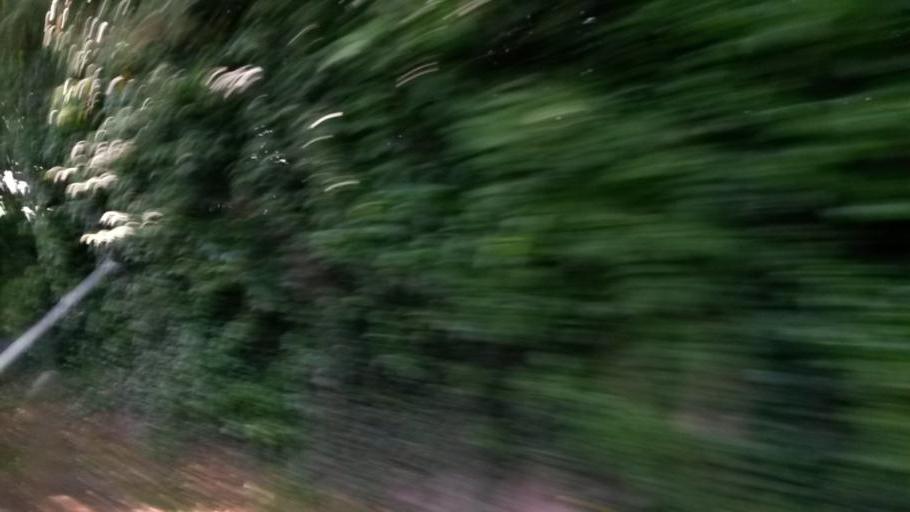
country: IE
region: Leinster
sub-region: An Mhi
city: Slane
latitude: 53.7150
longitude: -6.5388
